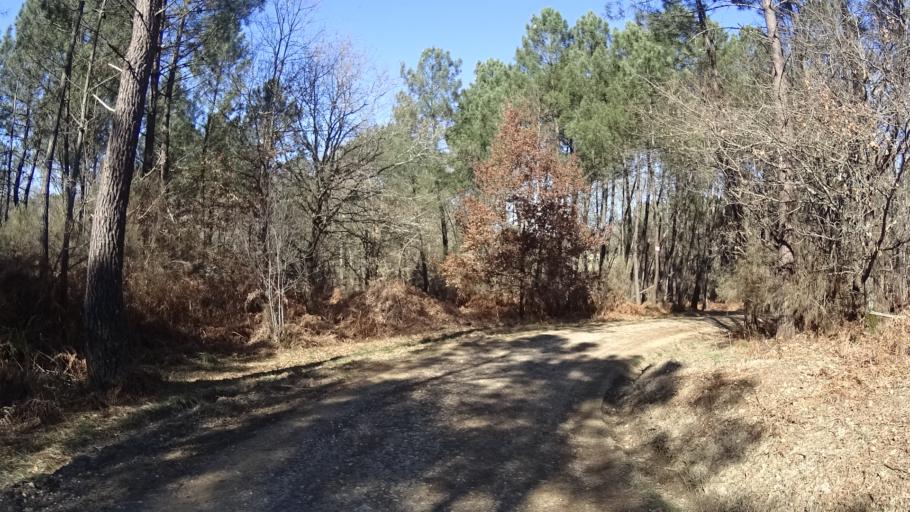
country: FR
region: Aquitaine
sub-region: Departement de la Dordogne
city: Riberac
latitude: 45.1896
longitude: 0.3089
